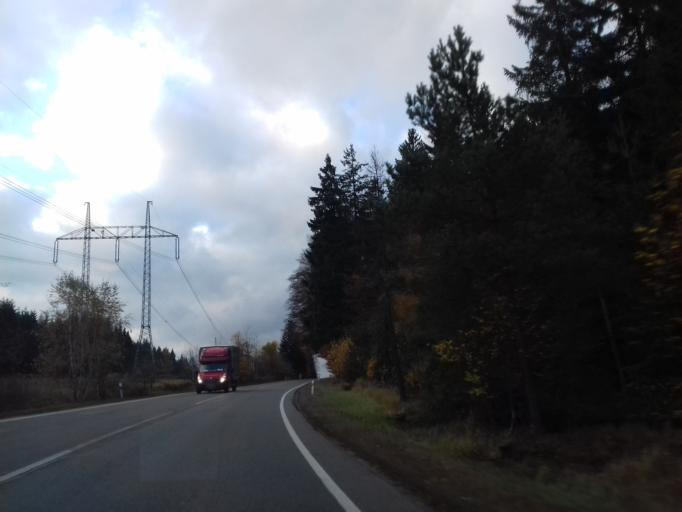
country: CZ
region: Pardubicky
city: Prosec
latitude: 49.7485
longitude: 16.1440
